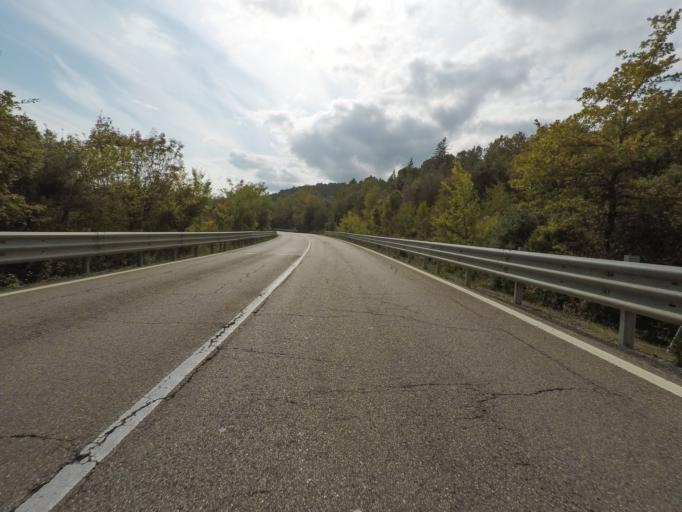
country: IT
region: Tuscany
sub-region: Provincia di Siena
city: Murlo
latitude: 43.1348
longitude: 11.2905
